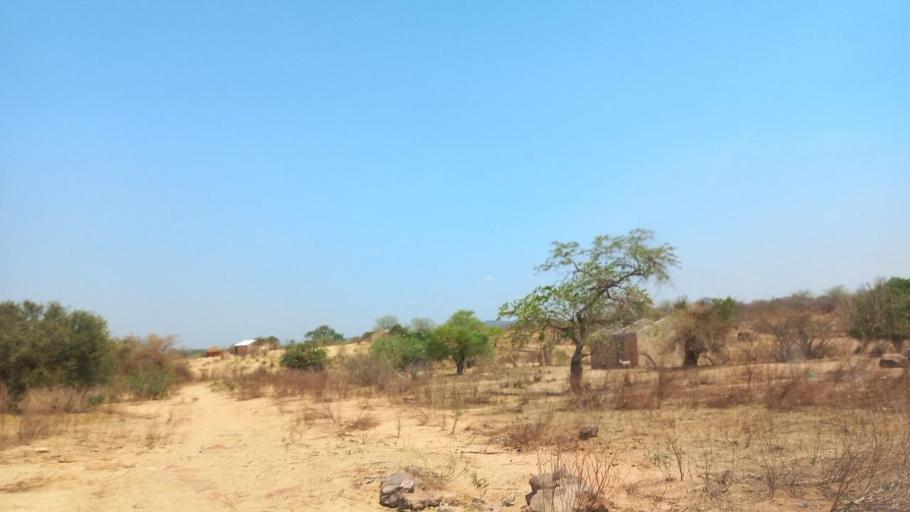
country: ZM
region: Lusaka
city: Luangwa
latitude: -15.5912
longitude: 30.3977
